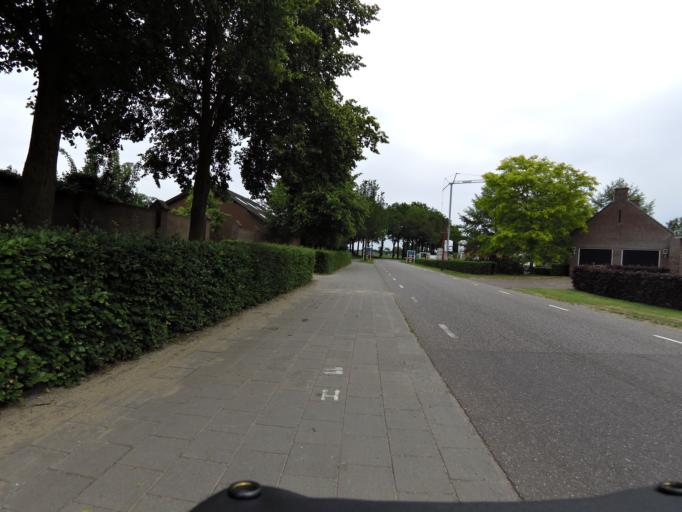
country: NL
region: North Brabant
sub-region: Gemeente Hilvarenbeek
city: Hilvarenbeek
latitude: 51.4786
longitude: 5.1845
